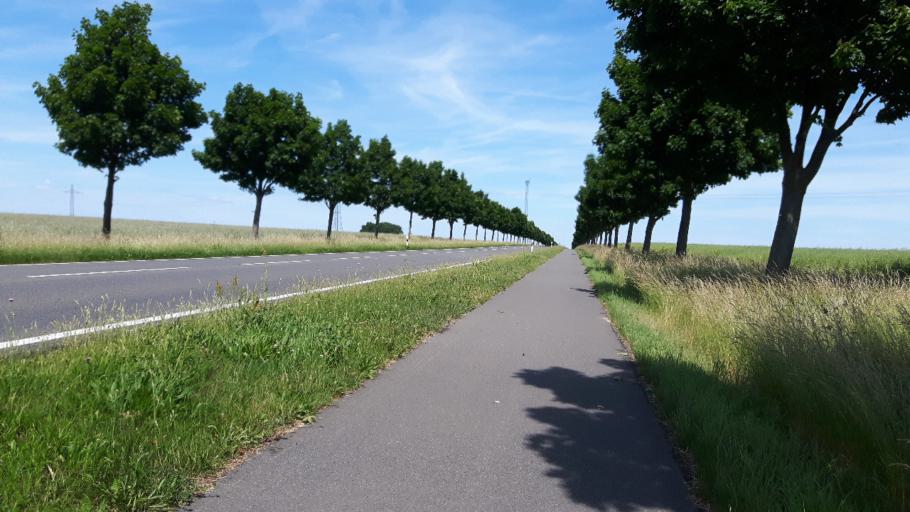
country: DE
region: Saxony-Anhalt
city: Kropstadt
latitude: 52.0182
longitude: 12.7924
